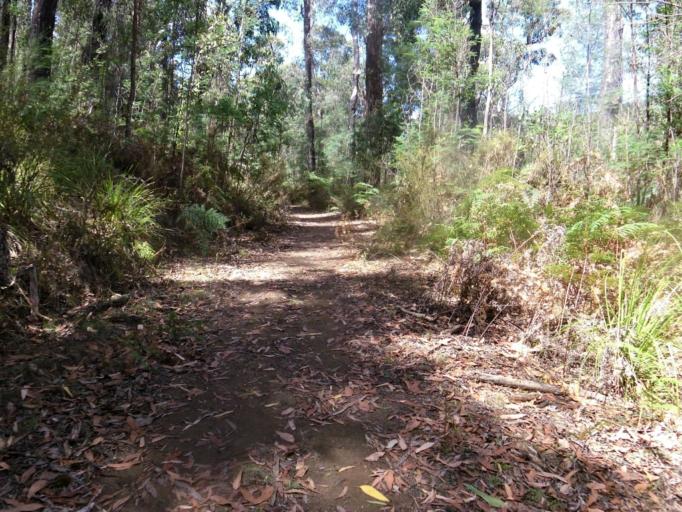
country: AU
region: Victoria
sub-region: Yarra Ranges
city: Healesville
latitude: -37.4215
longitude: 145.5671
